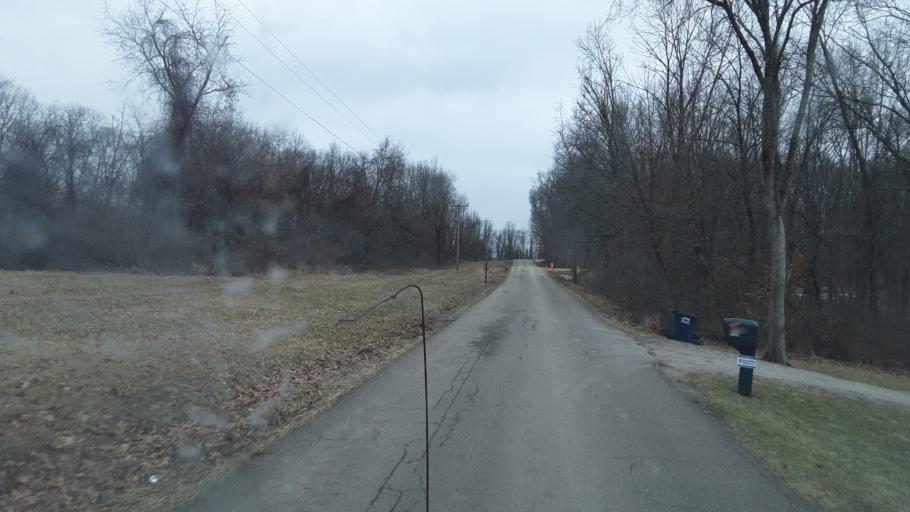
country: US
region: Ohio
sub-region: Perry County
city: Thornport
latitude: 39.9390
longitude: -82.3702
